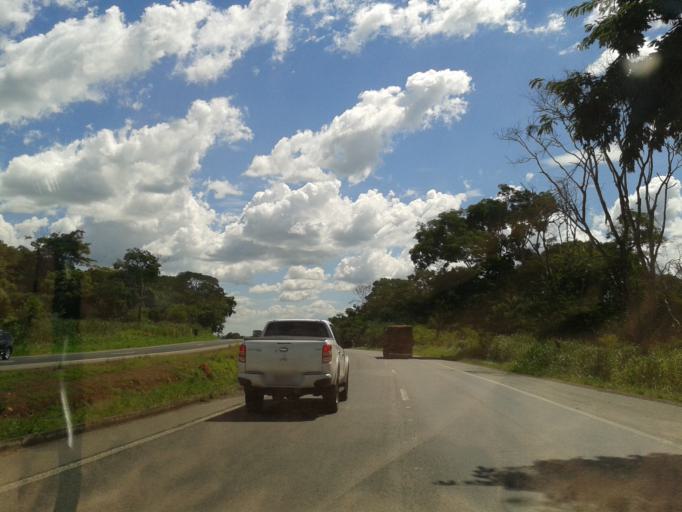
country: BR
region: Goias
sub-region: Piracanjuba
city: Piracanjuba
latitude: -17.3436
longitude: -49.2466
